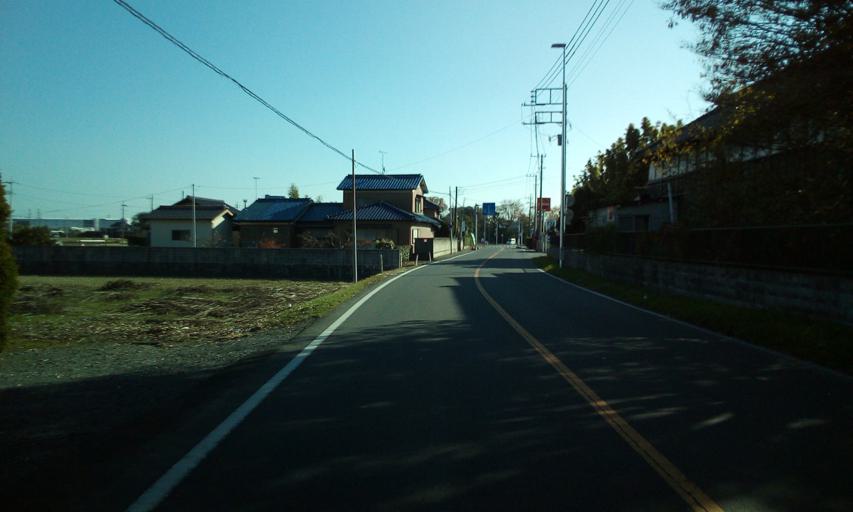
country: JP
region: Ibaraki
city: Sakai
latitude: 36.0518
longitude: 139.7774
